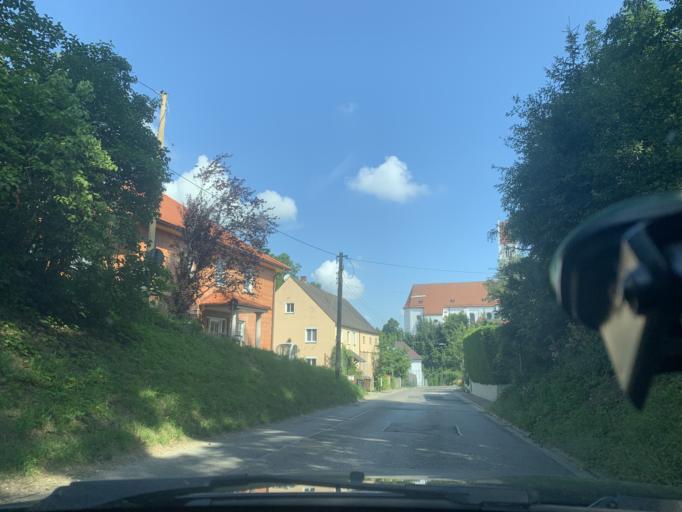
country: DE
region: Bavaria
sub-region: Swabia
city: Kissing
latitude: 48.2952
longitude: 10.9899
